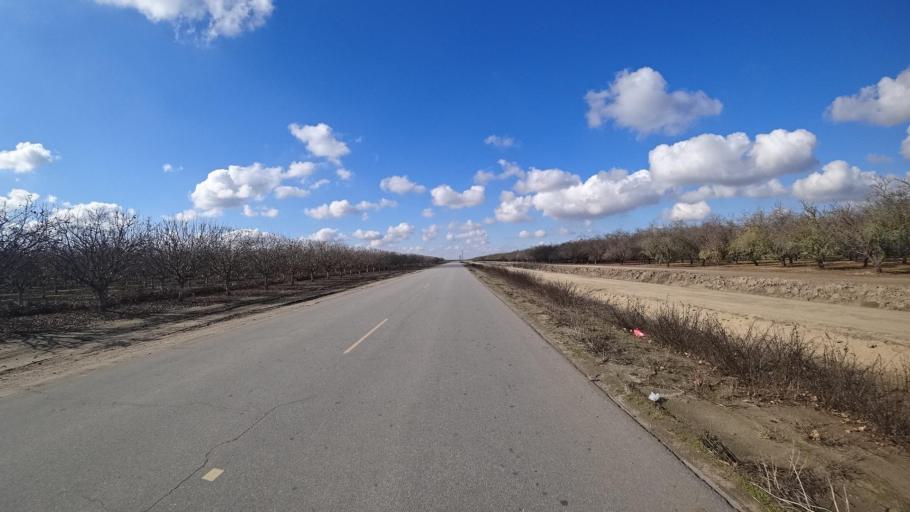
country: US
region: California
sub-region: Kern County
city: Wasco
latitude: 35.6741
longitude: -119.3211
